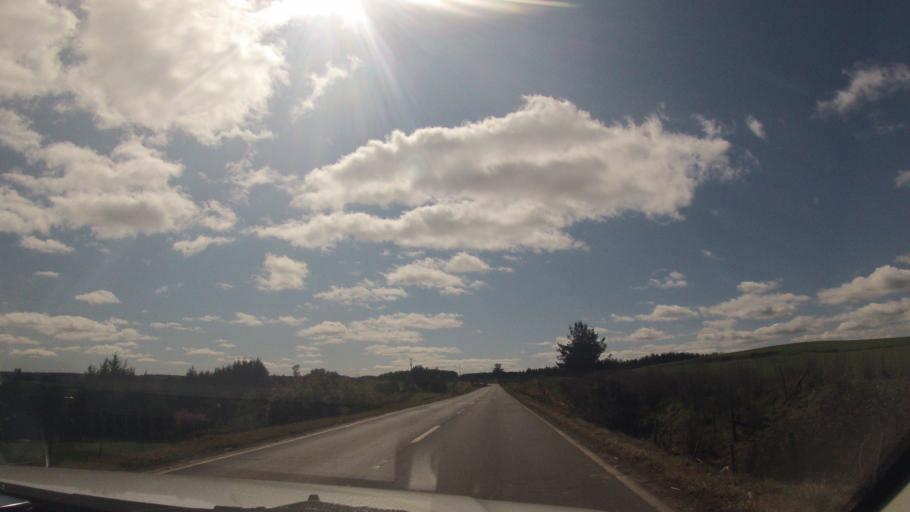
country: CL
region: Araucania
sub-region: Provincia de Malleco
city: Traiguen
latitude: -38.2243
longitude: -72.7085
